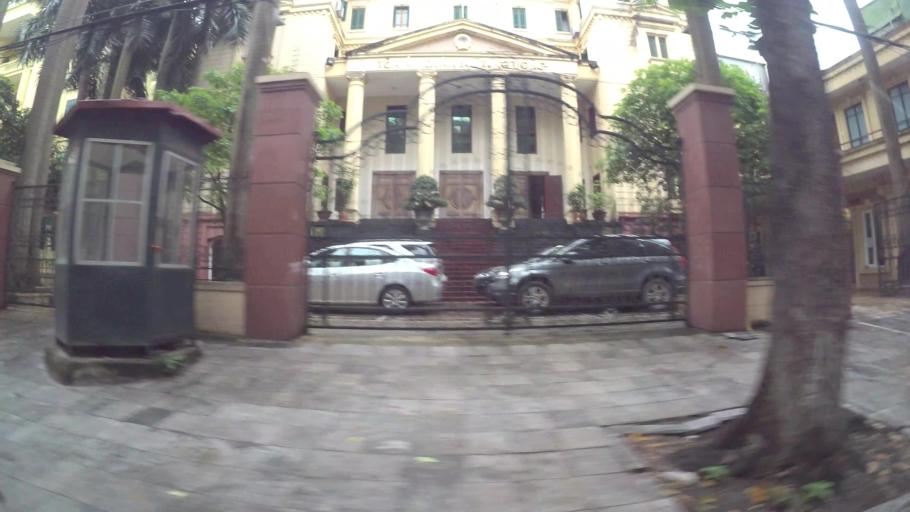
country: VN
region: Ha Noi
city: Hoan Kiem
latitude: 21.0366
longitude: 105.8452
